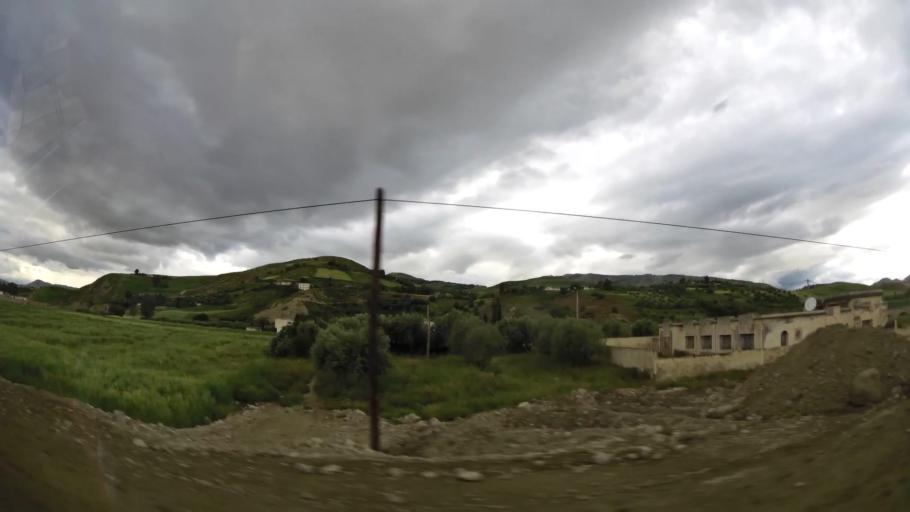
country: MA
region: Taza-Al Hoceima-Taounate
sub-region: Taza
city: Taza
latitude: 34.3507
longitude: -3.9212
